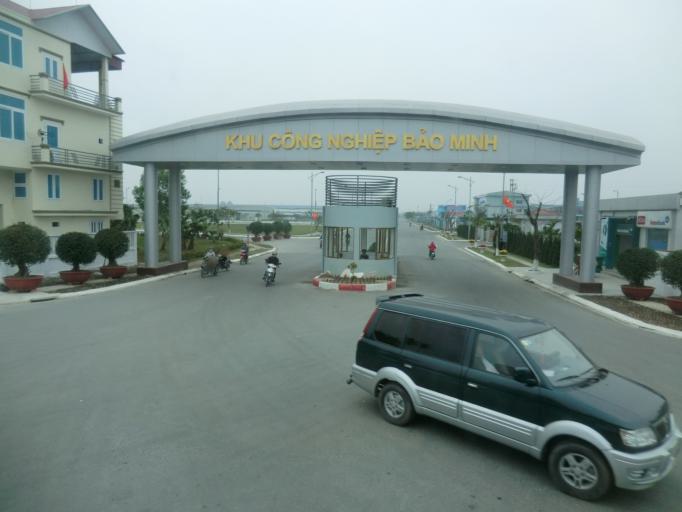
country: VN
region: Nam Dinh
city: Thi Tran Goi
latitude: 20.3488
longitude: 106.1106
